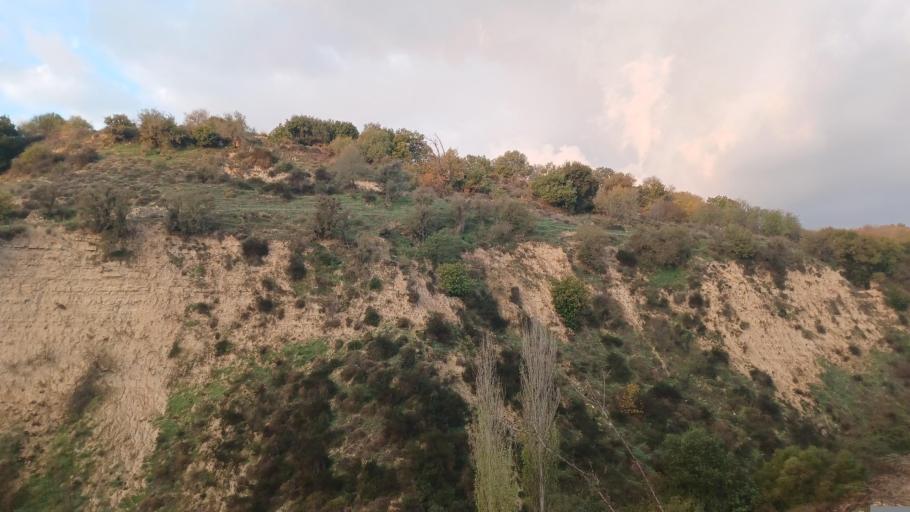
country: CY
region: Pafos
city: Mesogi
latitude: 34.8488
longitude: 32.5192
